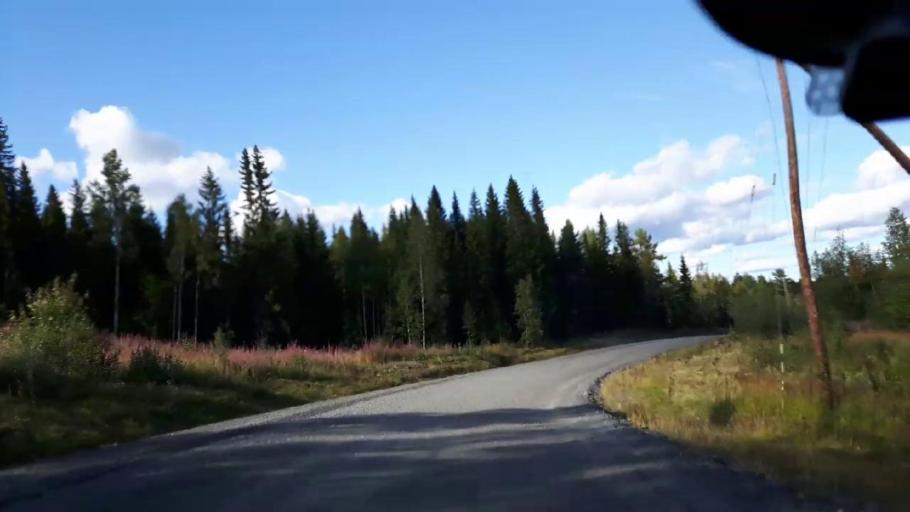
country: SE
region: Jaemtland
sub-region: Ragunda Kommun
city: Hammarstrand
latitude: 63.4317
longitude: 16.1806
